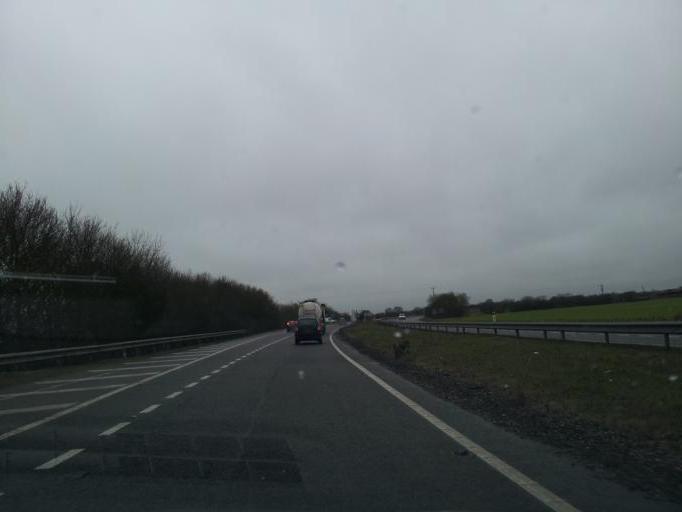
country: GB
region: England
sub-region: Essex
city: Great Bentley
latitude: 51.8875
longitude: 1.0604
